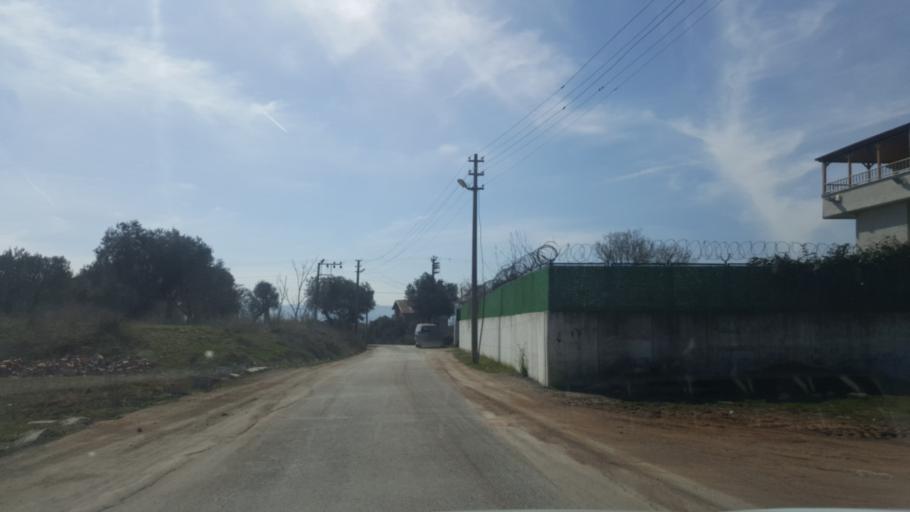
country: TR
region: Kocaeli
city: Tavsancil
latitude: 40.7756
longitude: 29.5717
